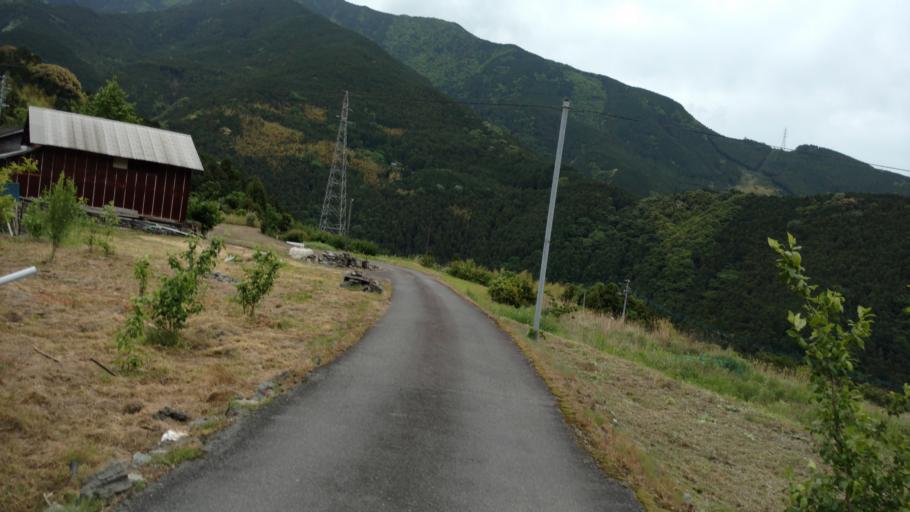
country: JP
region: Ehime
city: Saijo
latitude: 33.8631
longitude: 133.1970
